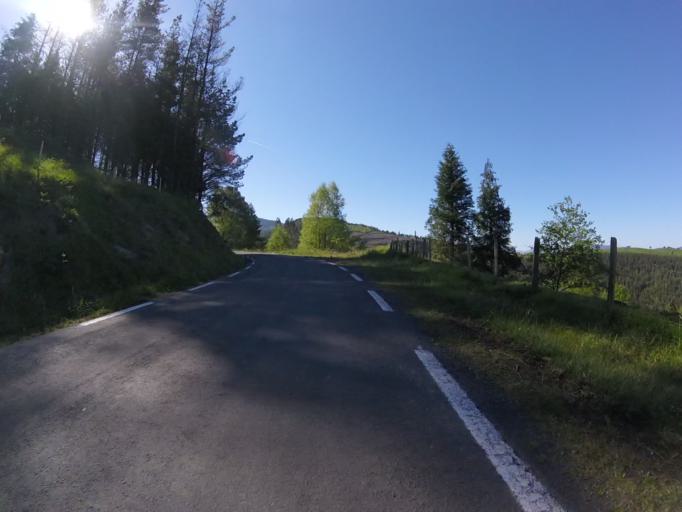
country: ES
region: Basque Country
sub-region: Provincia de Guipuzcoa
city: Errezil
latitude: 43.2079
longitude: -2.2000
